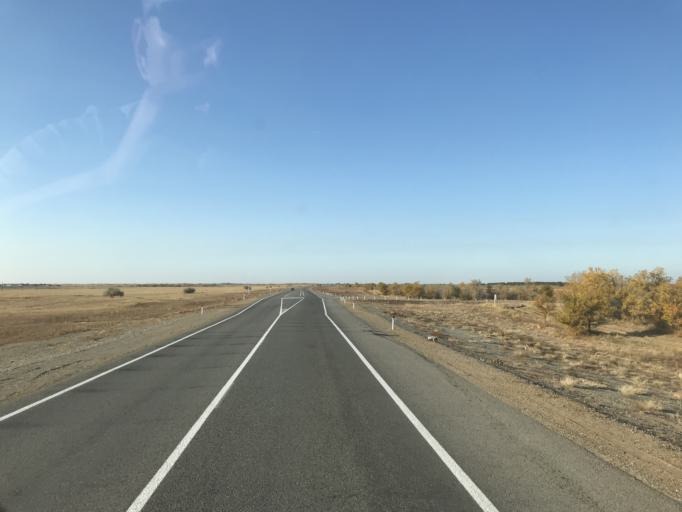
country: KZ
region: Pavlodar
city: Koktobe
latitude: 51.7994
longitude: 77.4827
